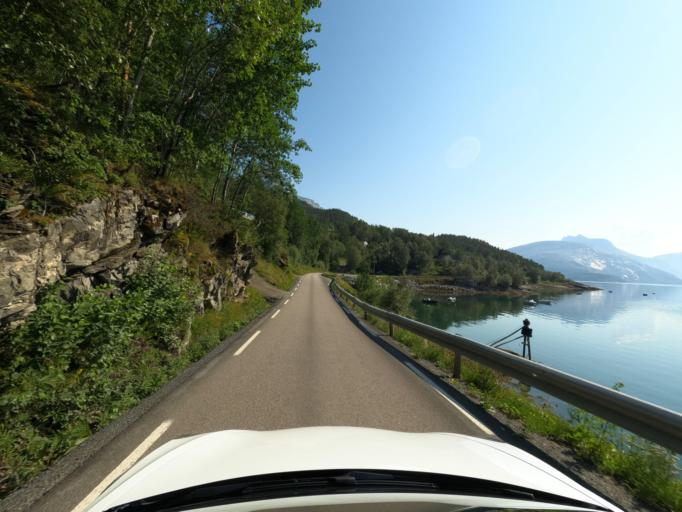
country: NO
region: Nordland
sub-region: Narvik
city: Narvik
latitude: 68.2967
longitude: 17.3544
